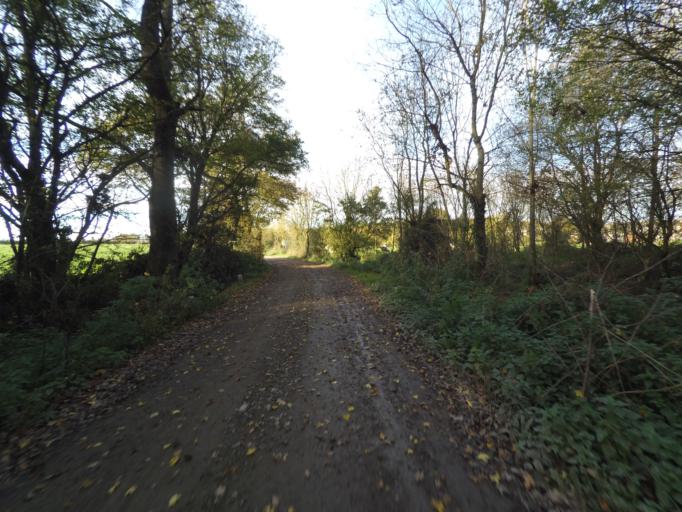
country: FR
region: Pays de la Loire
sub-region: Departement de la Vendee
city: Saint-Hilaire-de-Loulay
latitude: 47.0128
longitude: -1.3481
